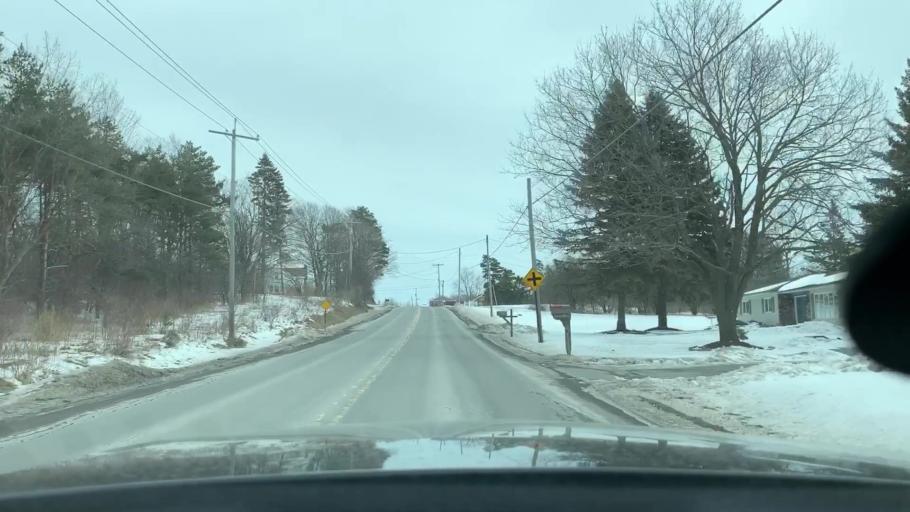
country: US
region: New York
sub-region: Oneida County
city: Washington Mills
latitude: 43.0501
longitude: -75.2359
